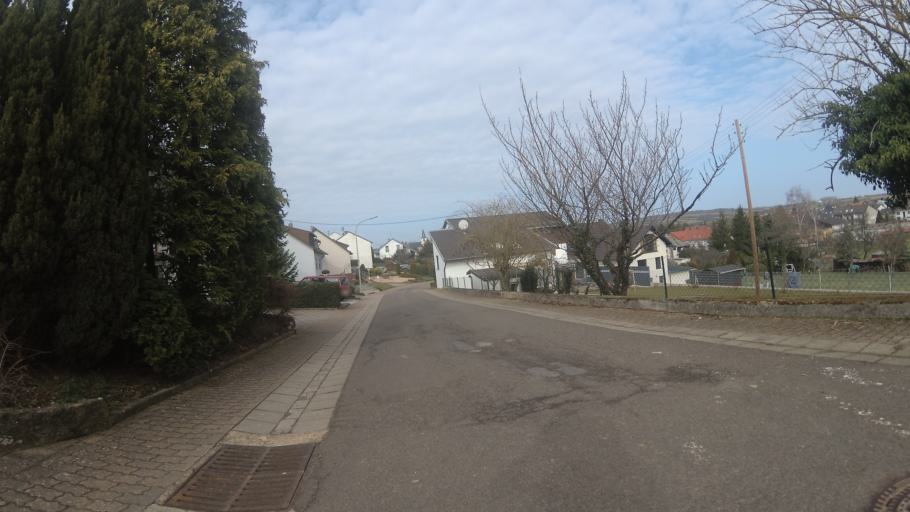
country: FR
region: Lorraine
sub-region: Departement de la Moselle
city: Merten
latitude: 49.2941
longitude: 6.6543
